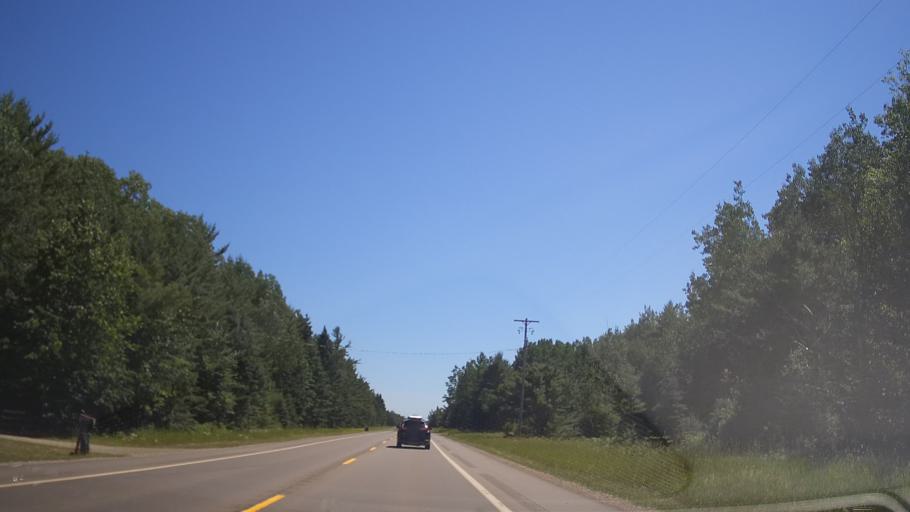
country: US
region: Michigan
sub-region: Cheboygan County
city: Indian River
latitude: 45.5868
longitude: -84.7831
